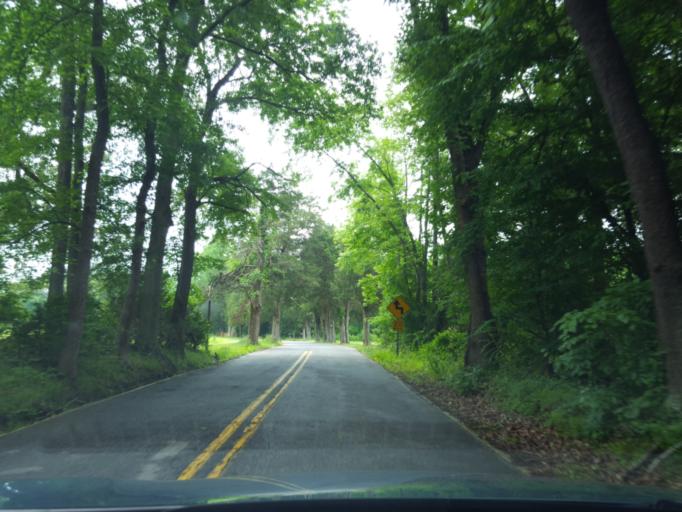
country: US
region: Maryland
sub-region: Prince George's County
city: Marlboro Meadows
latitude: 38.7860
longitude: -76.6872
